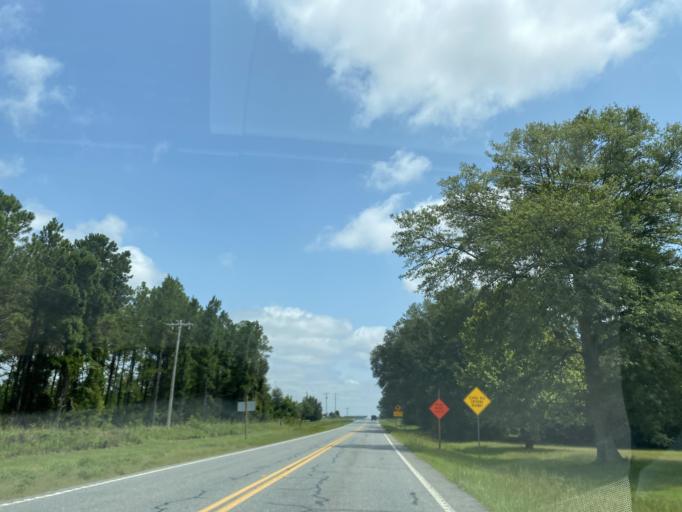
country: US
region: Georgia
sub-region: Telfair County
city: McRae
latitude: 32.0954
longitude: -82.8543
